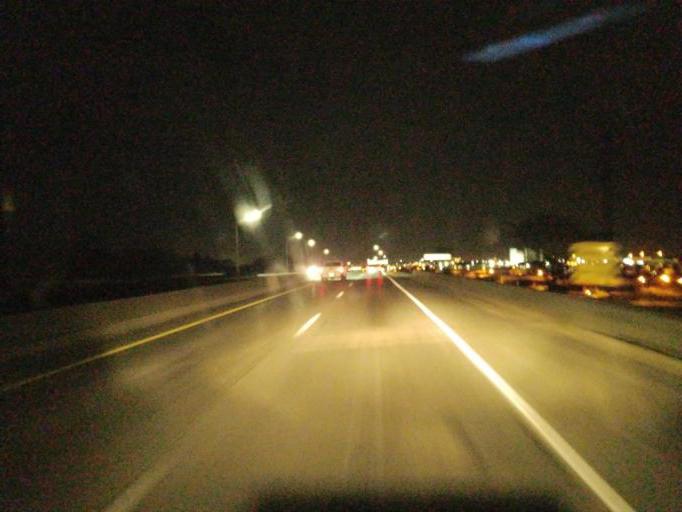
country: US
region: Iowa
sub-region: Dallas County
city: Waukee
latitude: 41.5868
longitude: -93.8190
